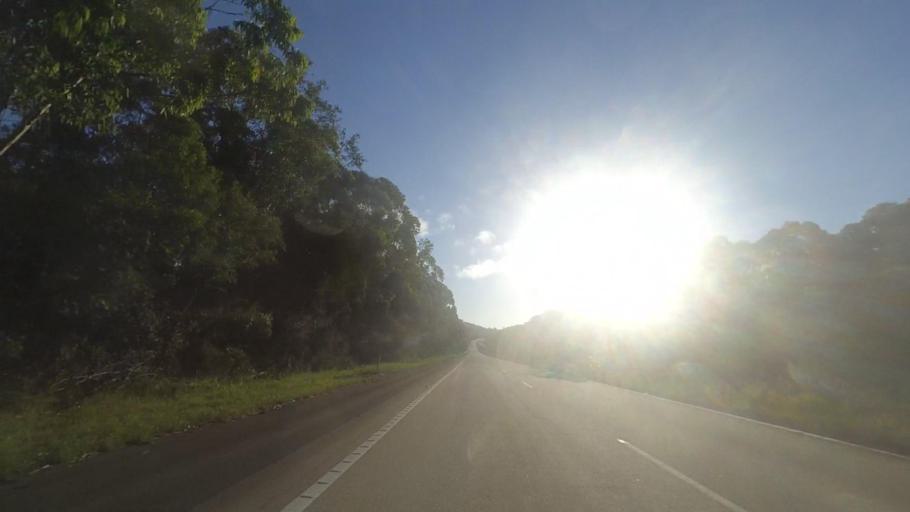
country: AU
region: New South Wales
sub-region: Great Lakes
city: Bulahdelah
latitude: -32.3803
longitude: 152.2693
